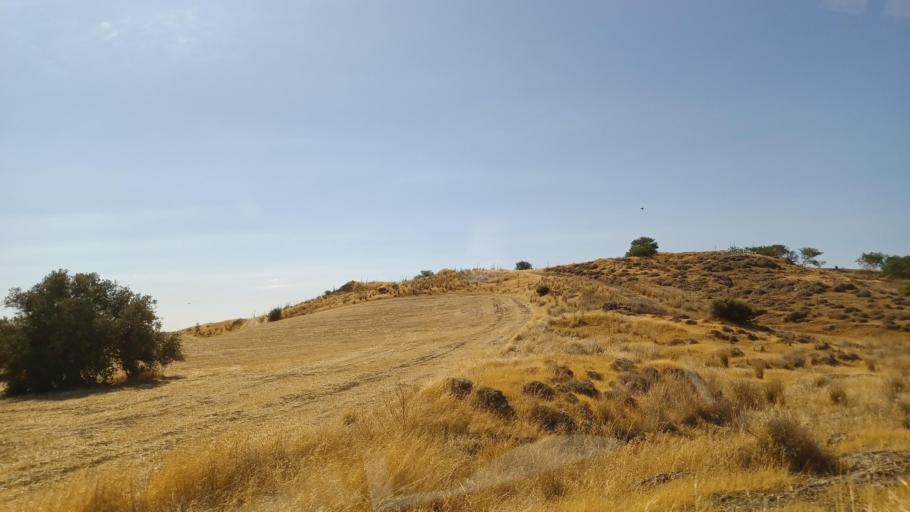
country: CY
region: Larnaka
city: Troulloi
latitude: 35.0125
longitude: 33.5864
